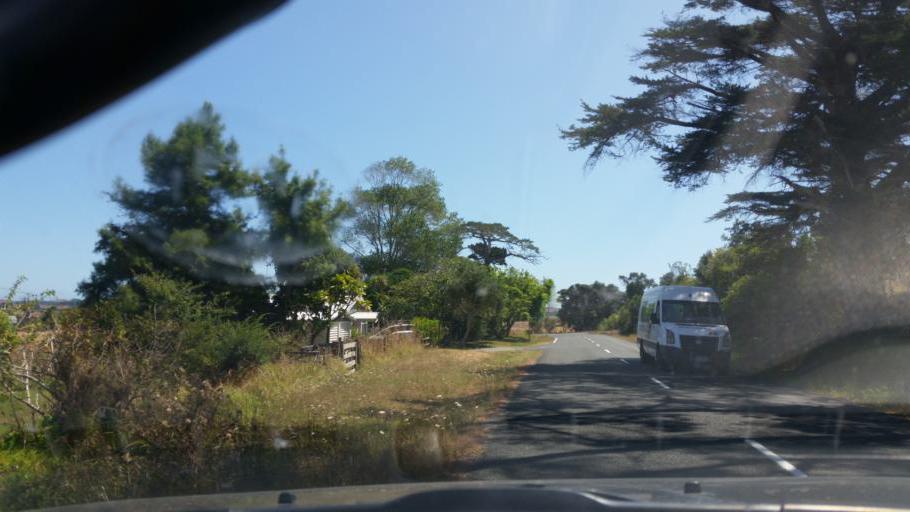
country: NZ
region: Northland
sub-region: Kaipara District
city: Dargaville
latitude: -36.0111
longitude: 173.9408
